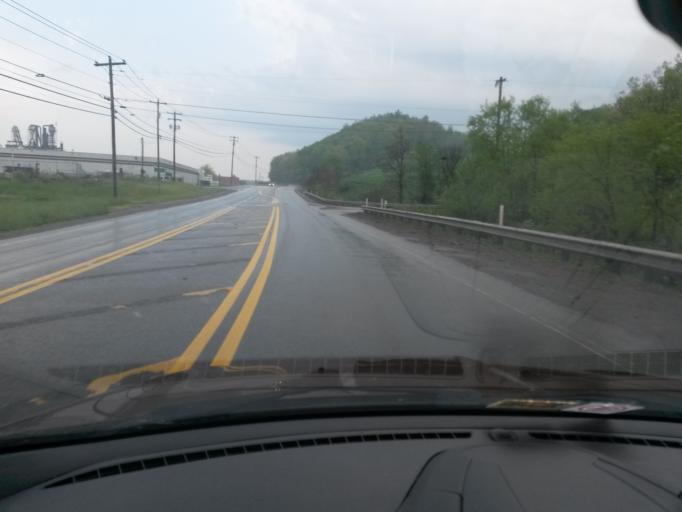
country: US
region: West Virginia
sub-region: Randolph County
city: Elkins
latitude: 38.8140
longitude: -79.8775
